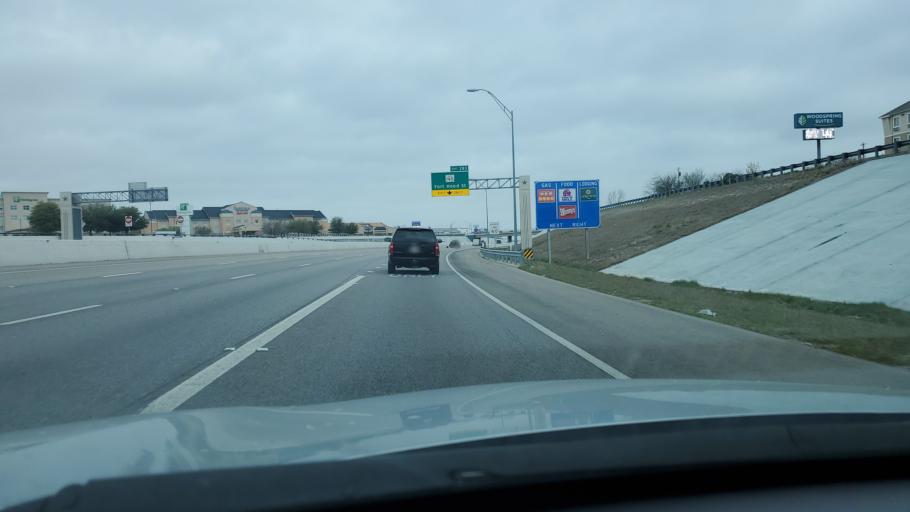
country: US
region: Texas
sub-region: Bell County
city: Killeen
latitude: 31.0973
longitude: -97.7377
